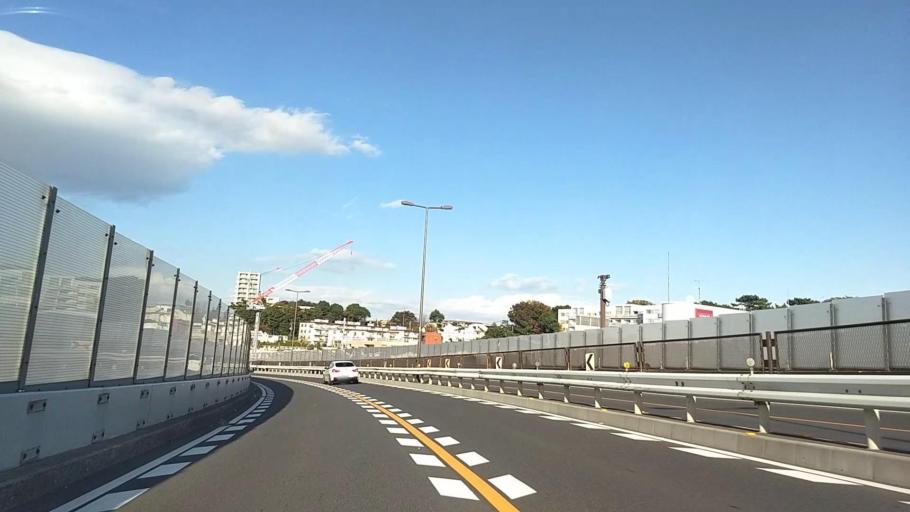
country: JP
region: Tokyo
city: Chofugaoka
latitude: 35.6156
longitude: 139.6273
